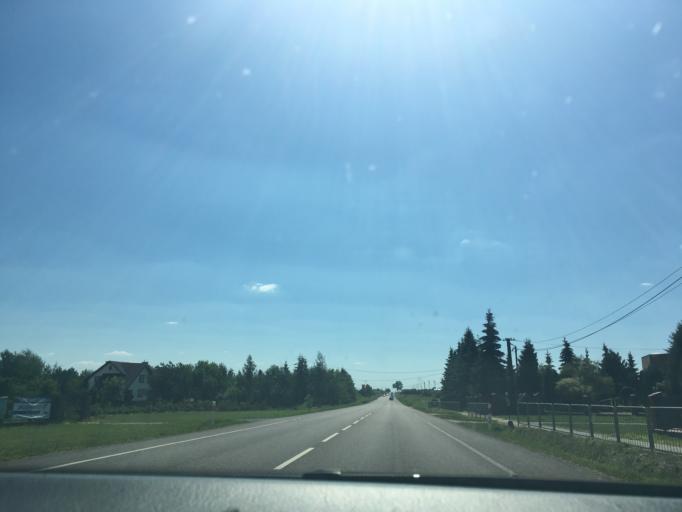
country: PL
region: Lublin Voivodeship
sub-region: Powiat janowski
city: Modliborzyce
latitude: 50.7486
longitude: 22.3374
